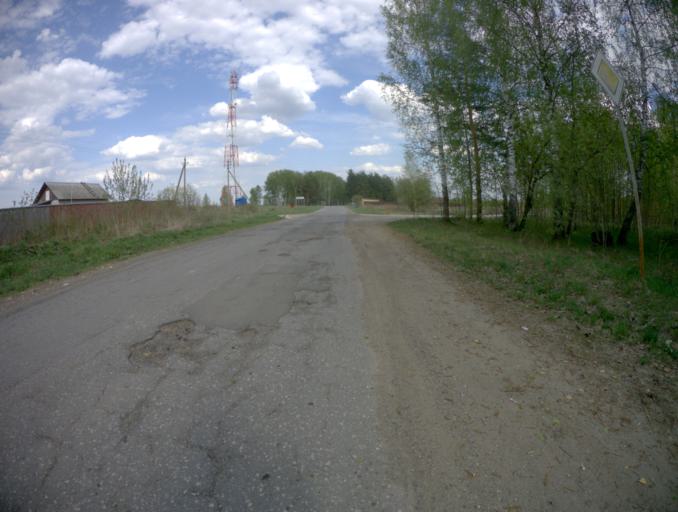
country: RU
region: Vladimir
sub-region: Kovrovskiy Rayon
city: Kovrov
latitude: 56.4429
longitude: 41.3053
